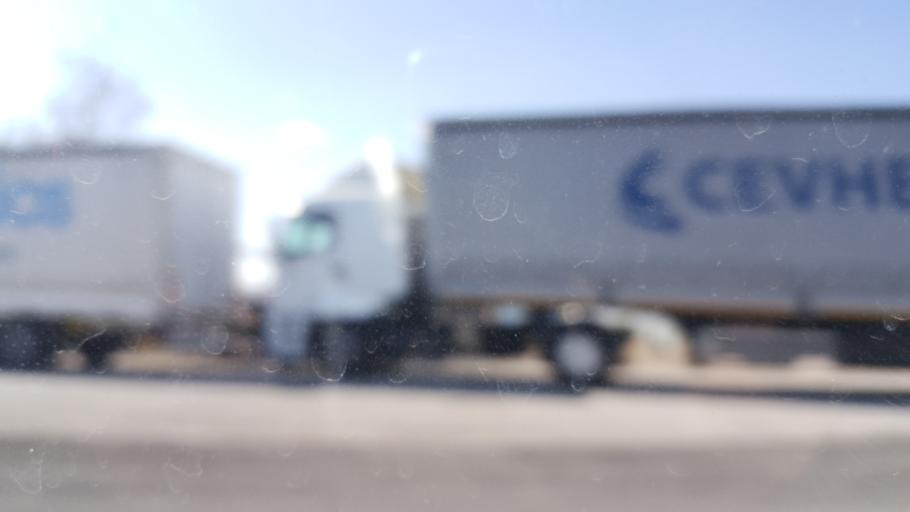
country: TR
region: Ankara
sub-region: Goelbasi
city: Golbasi
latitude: 39.7854
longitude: 32.8051
